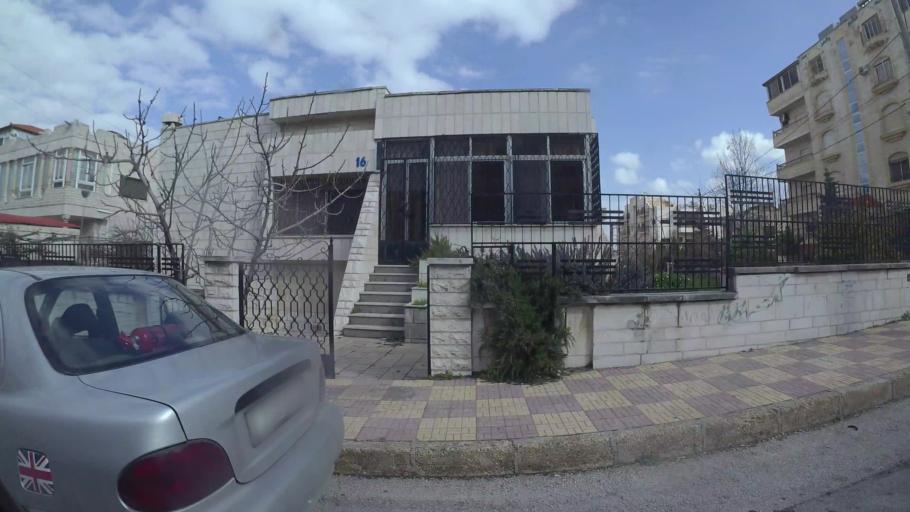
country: JO
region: Amman
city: Al Jubayhah
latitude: 32.0216
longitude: 35.8572
